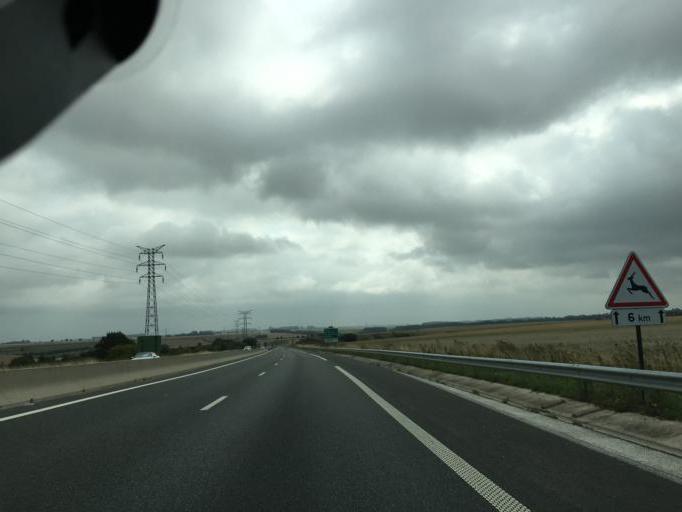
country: FR
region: Nord-Pas-de-Calais
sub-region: Departement du Pas-de-Calais
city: Montreuil
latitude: 50.4343
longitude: 1.7409
